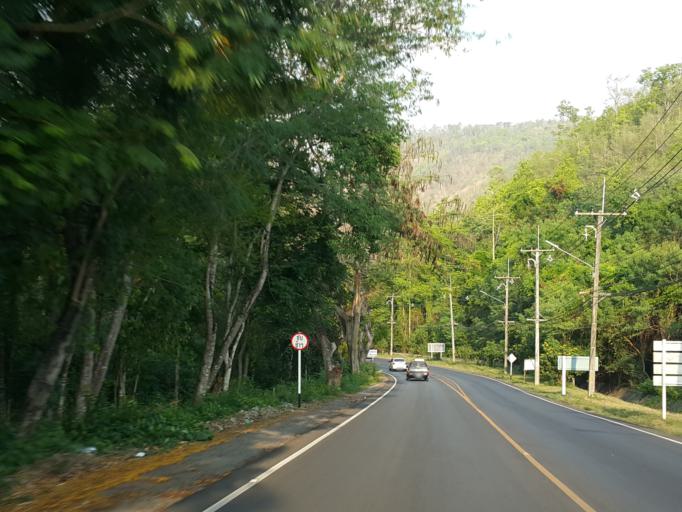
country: TH
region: Kanchanaburi
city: Si Sawat
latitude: 14.3845
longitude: 99.1387
